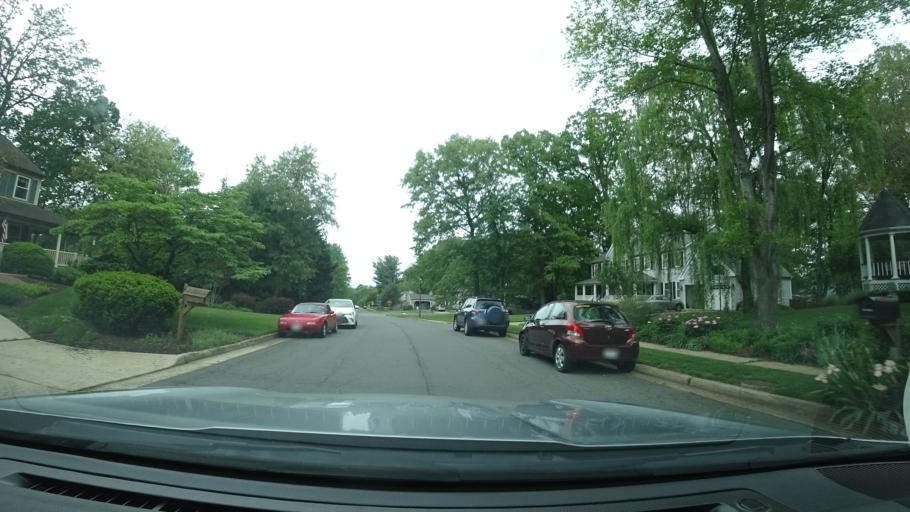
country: US
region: Virginia
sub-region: Fairfax County
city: Oak Hill
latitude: 38.9143
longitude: -77.3806
